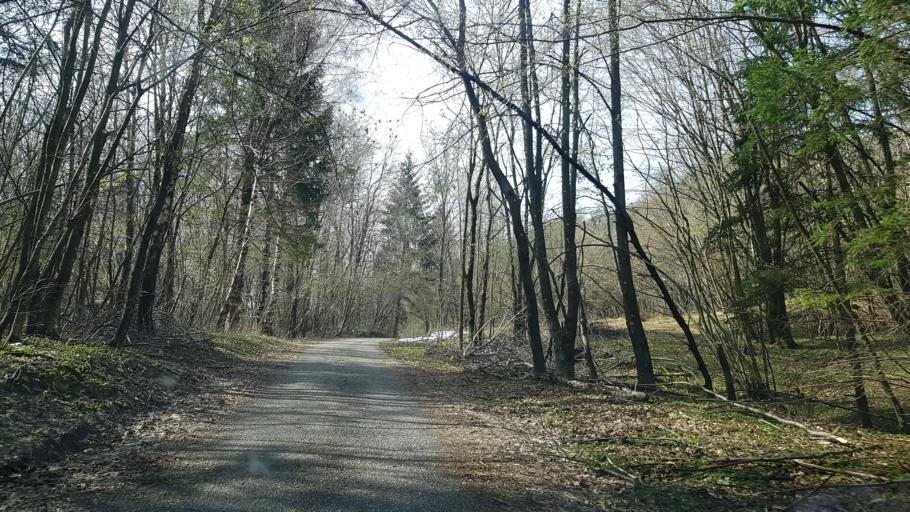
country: IT
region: Friuli Venezia Giulia
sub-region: Provincia di Udine
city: Trasaghis
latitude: 46.2853
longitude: 13.0155
